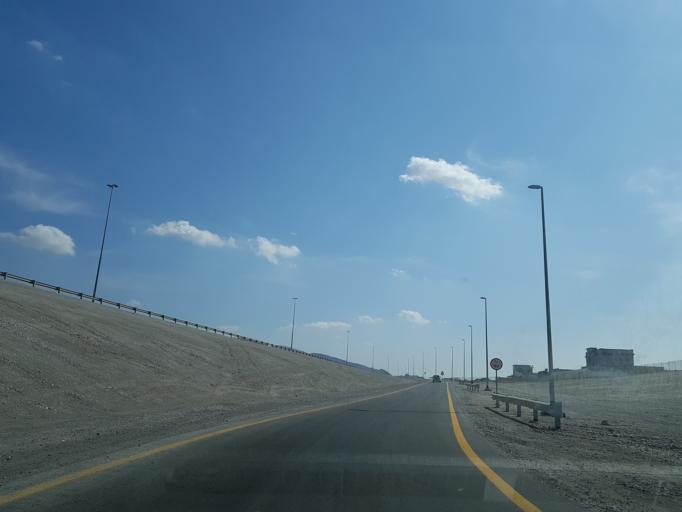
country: AE
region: Ra's al Khaymah
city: Ras al-Khaimah
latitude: 25.7982
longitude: 56.0301
